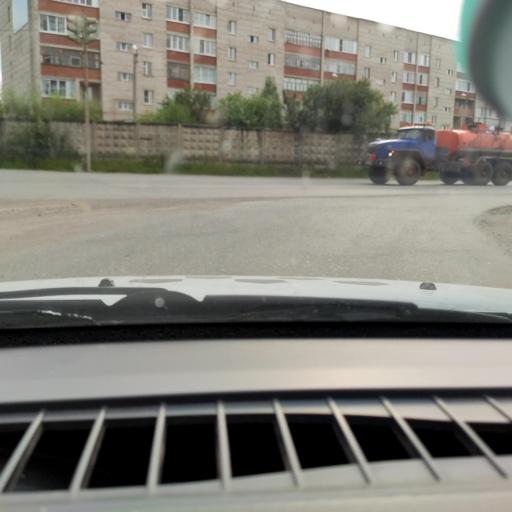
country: RU
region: Udmurtiya
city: Igra
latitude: 57.5517
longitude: 53.1055
